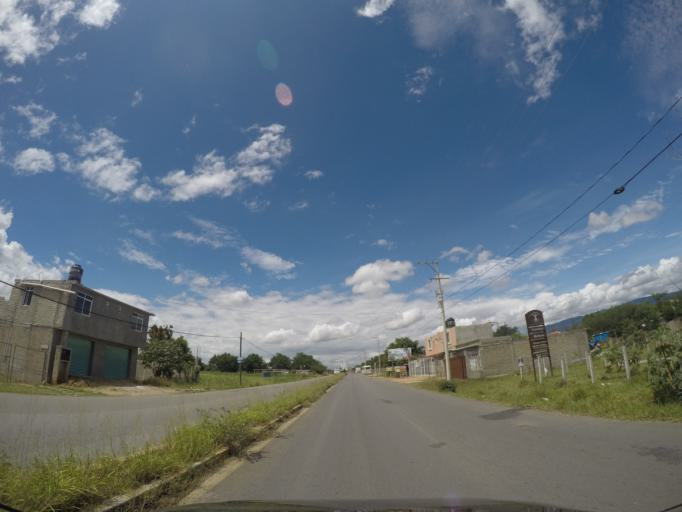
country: MX
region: Oaxaca
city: San Raymundo Jalpam
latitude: 16.9832
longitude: -96.7479
